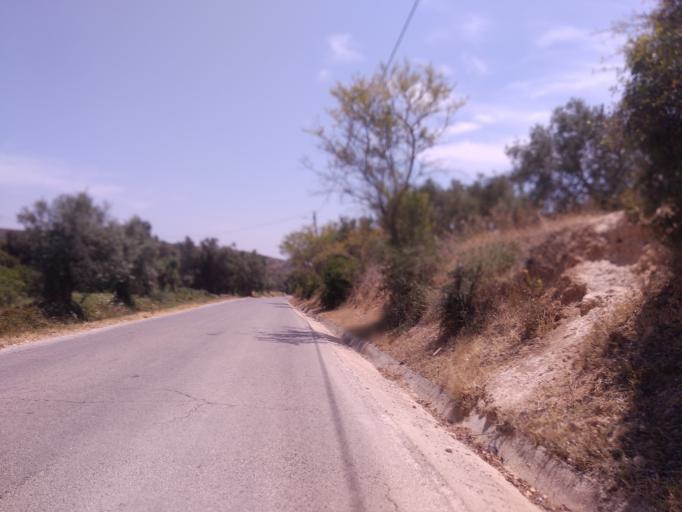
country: PT
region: Faro
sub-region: Faro
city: Santa Barbara de Nexe
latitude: 37.1148
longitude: -7.9454
